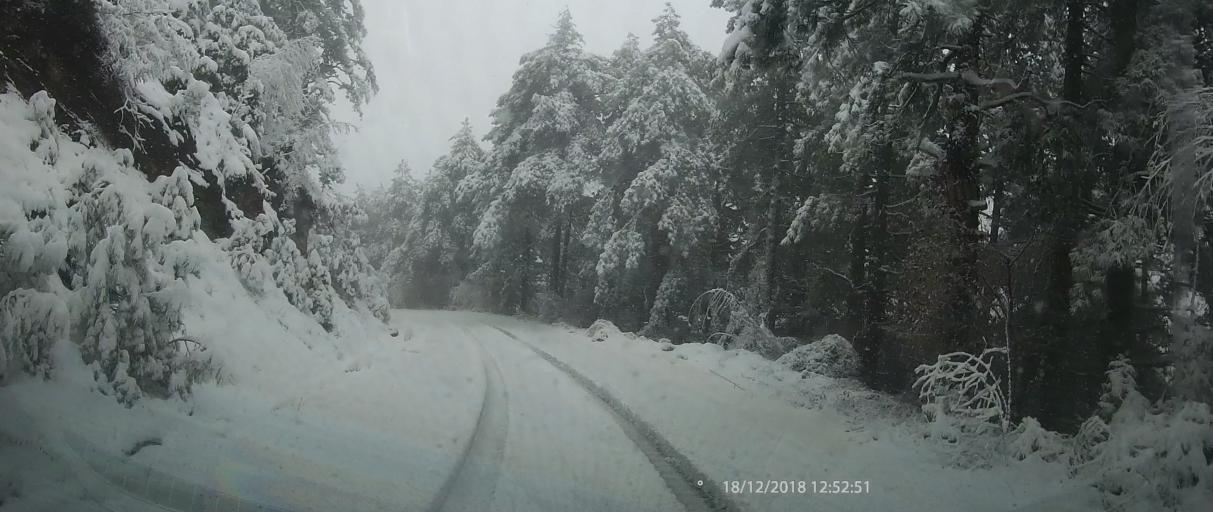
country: GR
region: Central Macedonia
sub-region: Nomos Pierias
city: Litochoro
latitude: 40.1032
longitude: 22.4526
